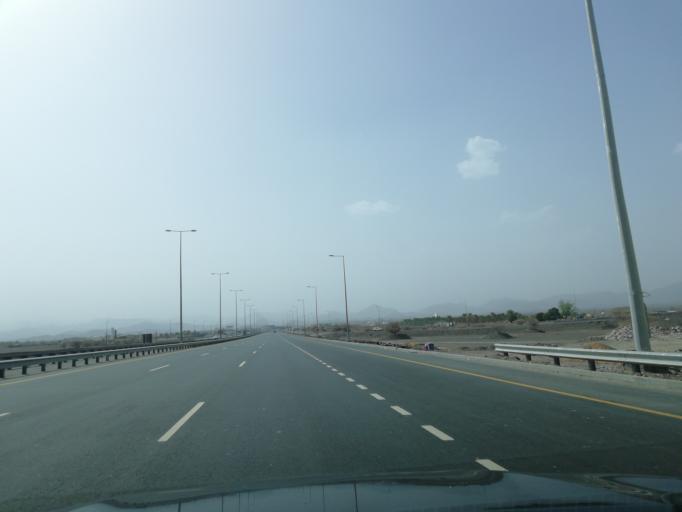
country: OM
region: Muhafazat ad Dakhiliyah
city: Sufalat Sama'il
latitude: 23.0181
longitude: 58.2181
